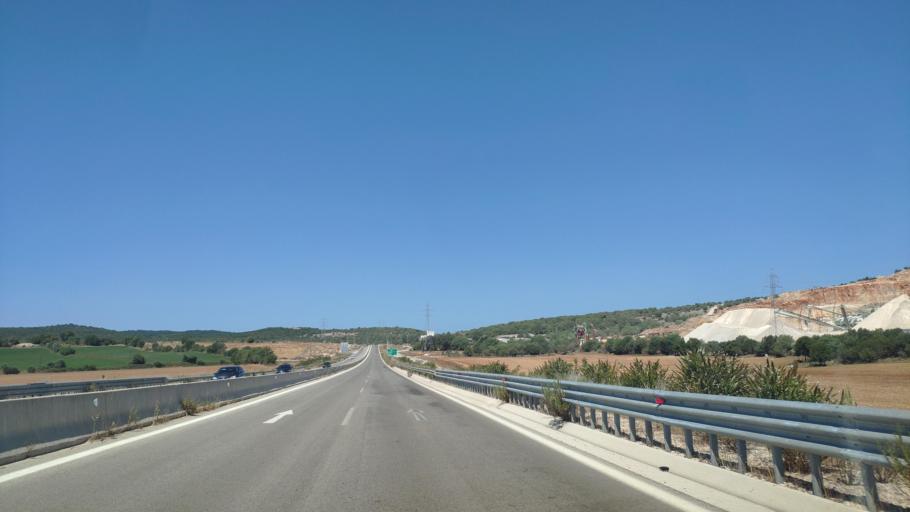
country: GR
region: West Greece
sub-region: Nomos Aitolias kai Akarnanias
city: Vonitsa
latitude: 38.9021
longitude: 20.8681
